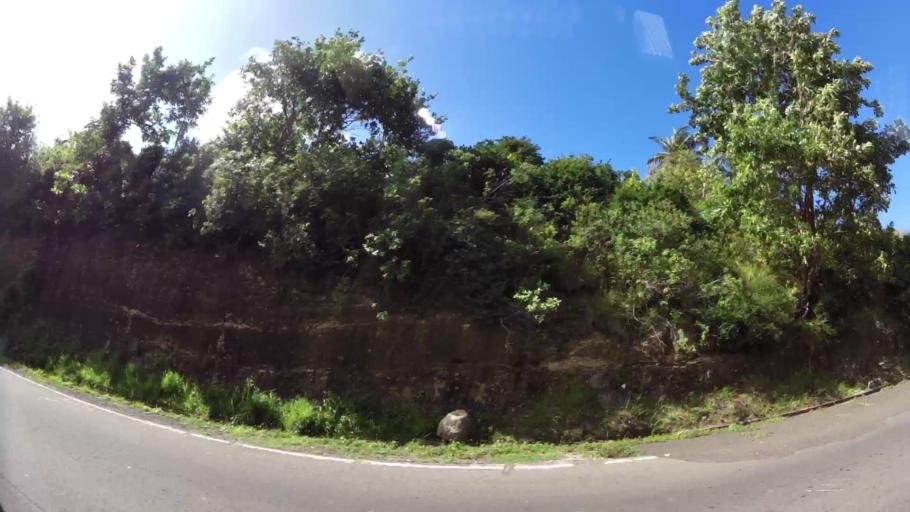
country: LC
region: Choiseul Quarter
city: Choiseul
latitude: 13.7938
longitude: -61.0383
